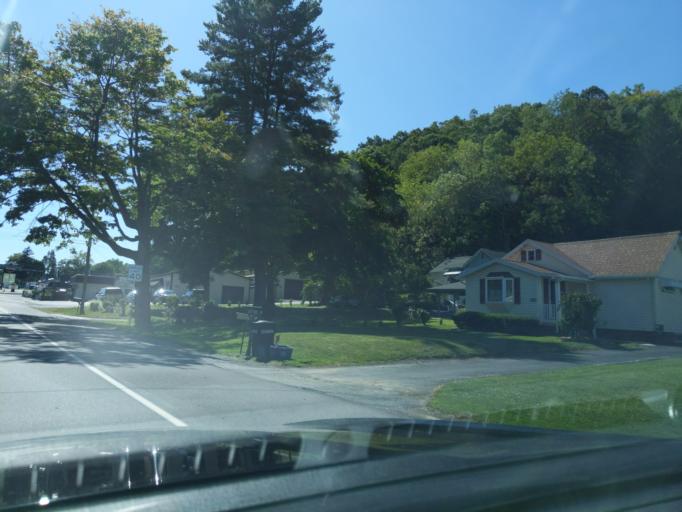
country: US
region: Pennsylvania
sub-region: Blair County
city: Greenwood
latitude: 40.5364
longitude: -78.3578
